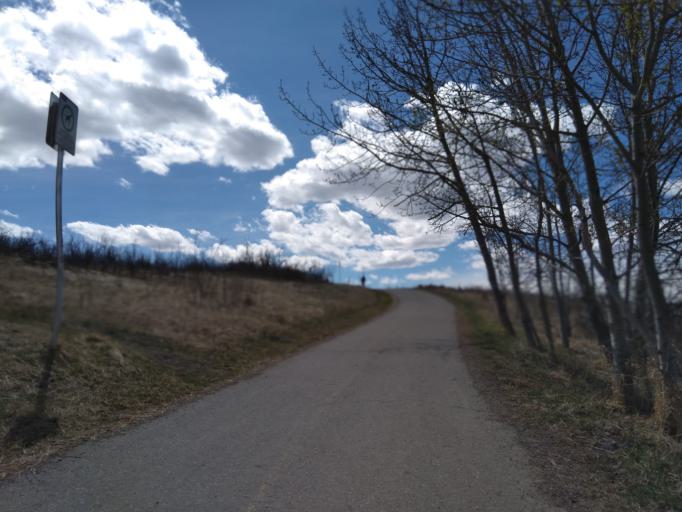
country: CA
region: Alberta
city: Calgary
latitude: 51.1016
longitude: -114.1906
